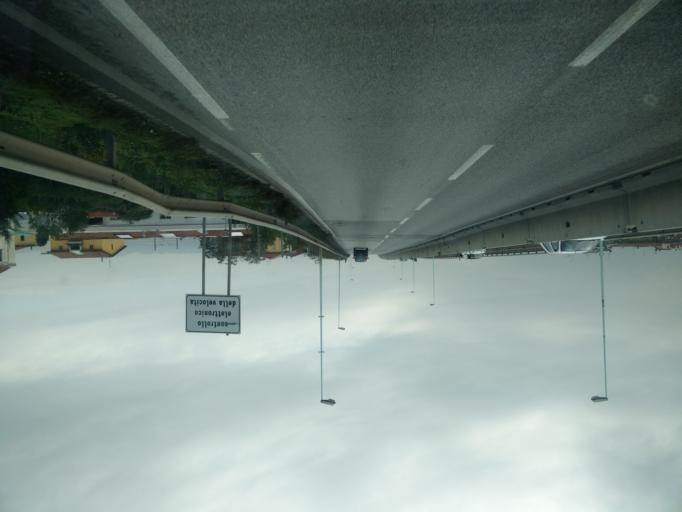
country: IT
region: Tuscany
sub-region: Provincia di Prato
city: Prato
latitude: 43.8929
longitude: 11.0741
